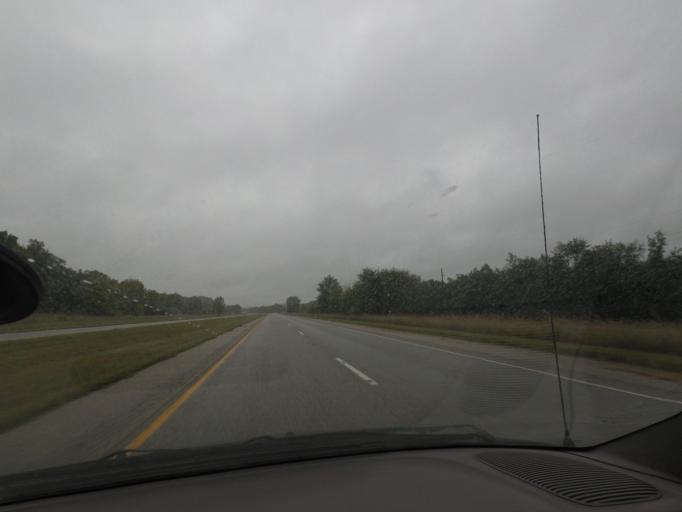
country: US
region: Illinois
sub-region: Pike County
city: Barry
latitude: 39.7138
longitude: -91.0857
